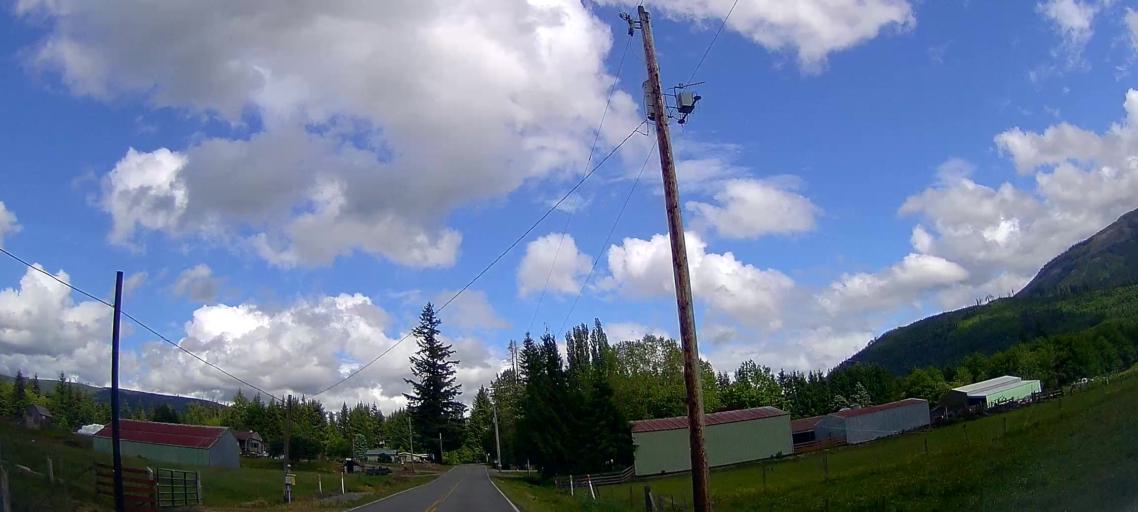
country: US
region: Washington
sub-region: Whatcom County
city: Sudden Valley
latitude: 48.6785
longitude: -122.1902
